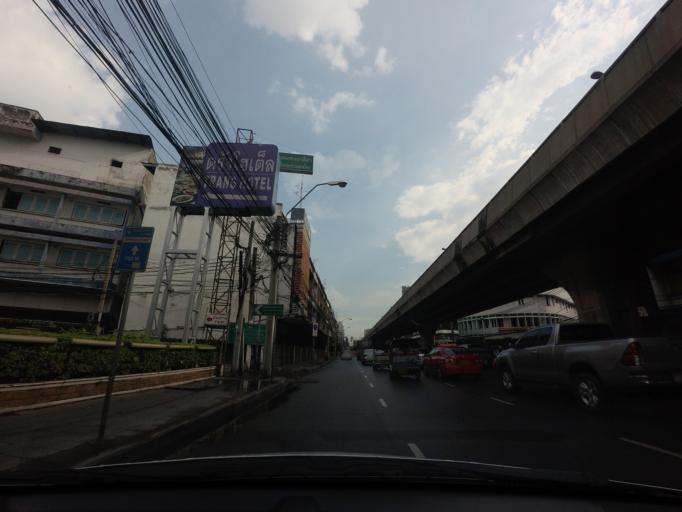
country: TH
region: Bangkok
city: Phra Nakhon
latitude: 13.7644
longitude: 100.5033
